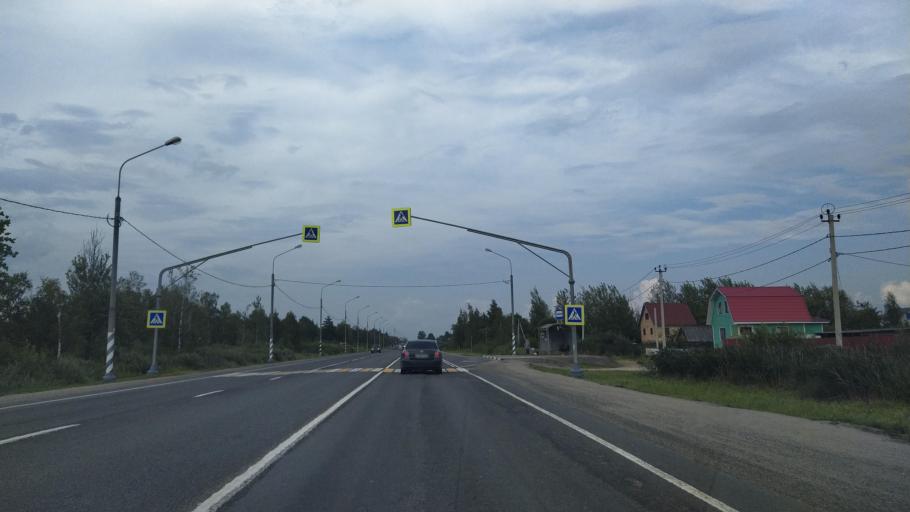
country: RU
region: Novgorod
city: Pankovka
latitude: 58.4842
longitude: 31.1913
